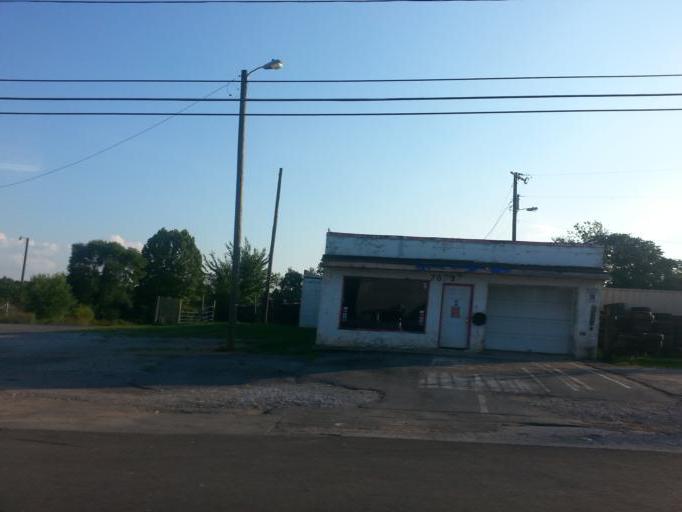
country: US
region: Tennessee
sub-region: Anderson County
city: Clinton
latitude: 36.0217
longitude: -84.0566
